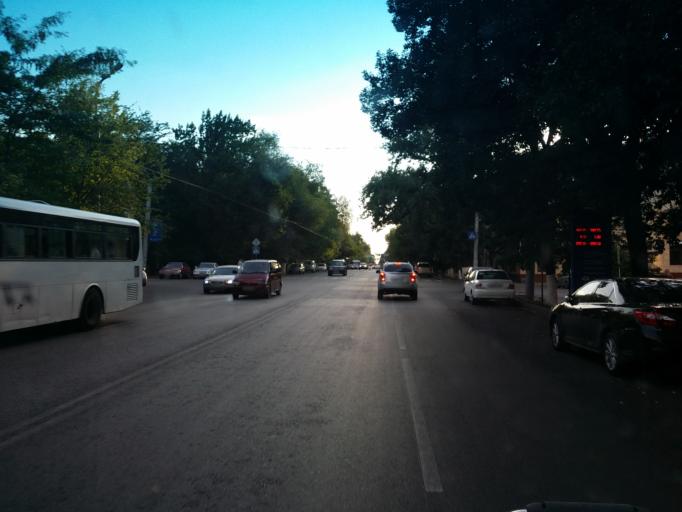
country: KZ
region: Almaty Qalasy
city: Almaty
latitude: 43.2607
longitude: 76.9571
